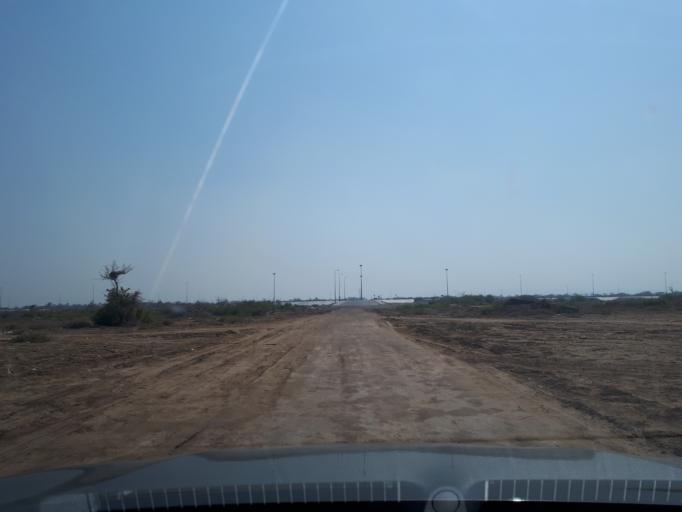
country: OM
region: Al Batinah
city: Shinas
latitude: 24.9190
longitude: 56.3919
